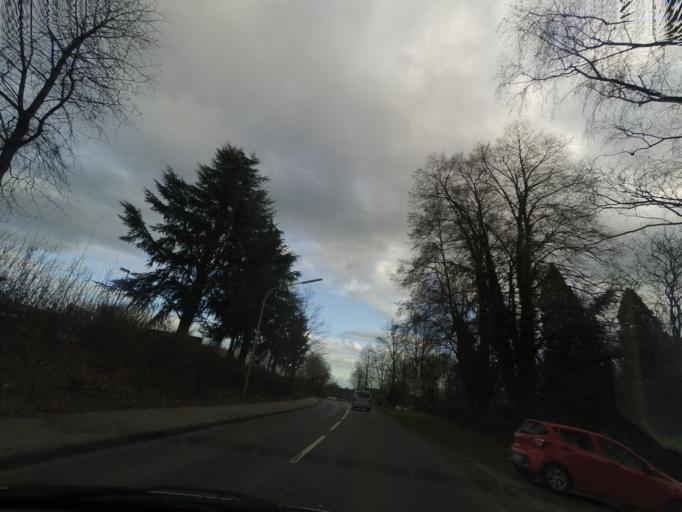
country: DE
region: North Rhine-Westphalia
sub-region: Regierungsbezirk Dusseldorf
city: Grevenbroich
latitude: 51.1081
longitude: 6.5767
